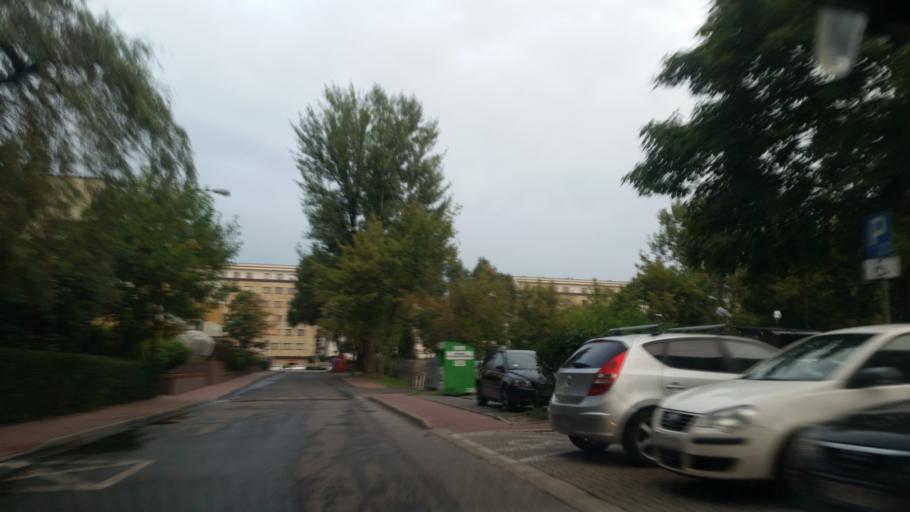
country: PL
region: Masovian Voivodeship
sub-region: Warszawa
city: Mokotow
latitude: 52.1811
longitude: 21.0524
